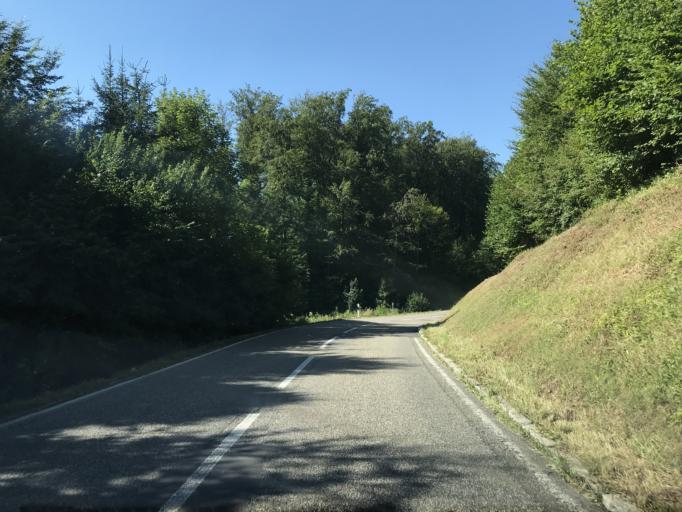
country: DE
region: Baden-Wuerttemberg
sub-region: Freiburg Region
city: Schopfheim
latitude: 47.6114
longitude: 7.8125
